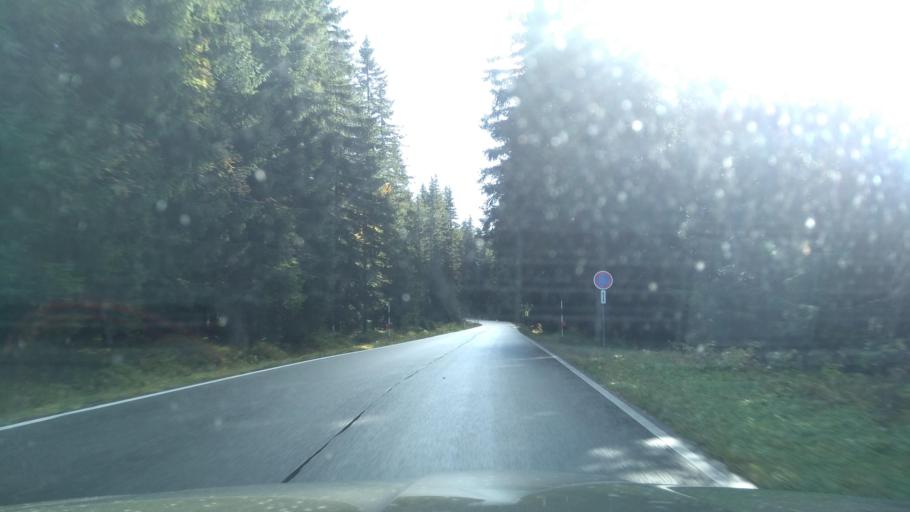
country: CZ
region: Plzensky
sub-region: Okres Klatovy
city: Kasperske Hory
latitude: 49.0291
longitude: 13.5281
